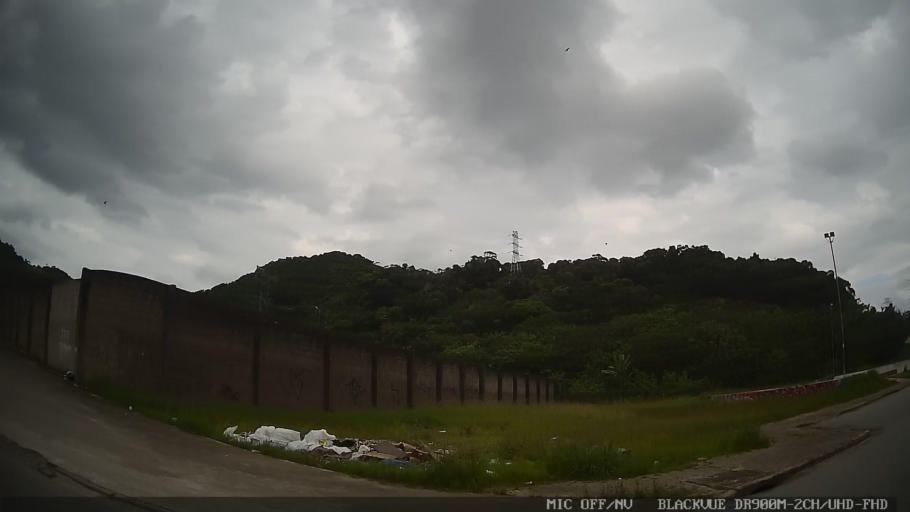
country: BR
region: Sao Paulo
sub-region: Guaruja
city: Guaruja
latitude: -23.9962
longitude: -46.2724
